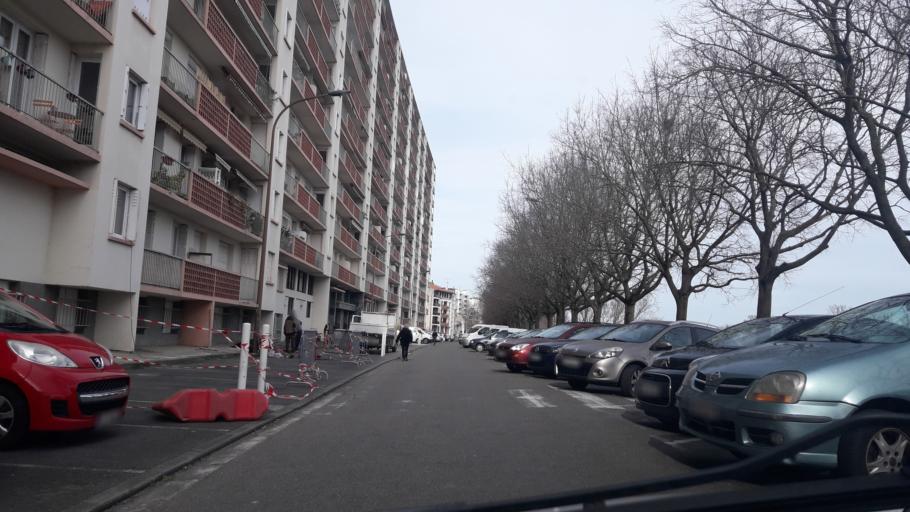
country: FR
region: Midi-Pyrenees
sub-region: Departement de la Haute-Garonne
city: Toulouse
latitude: 43.5819
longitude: 1.4278
